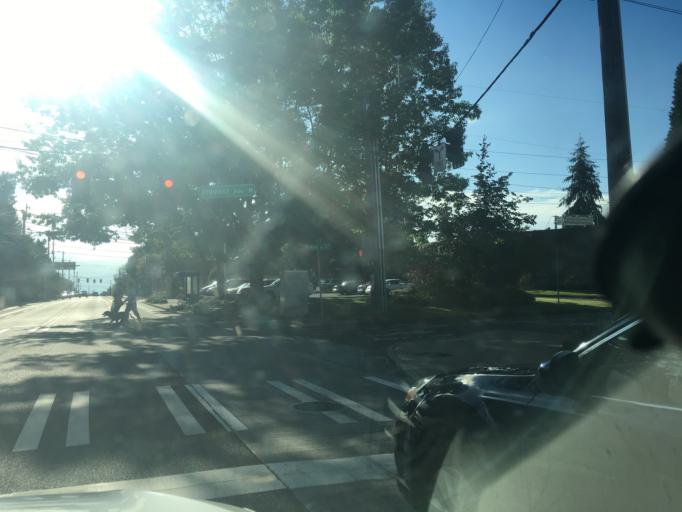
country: US
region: Washington
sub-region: King County
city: Shoreline
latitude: 47.7051
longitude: -122.3499
